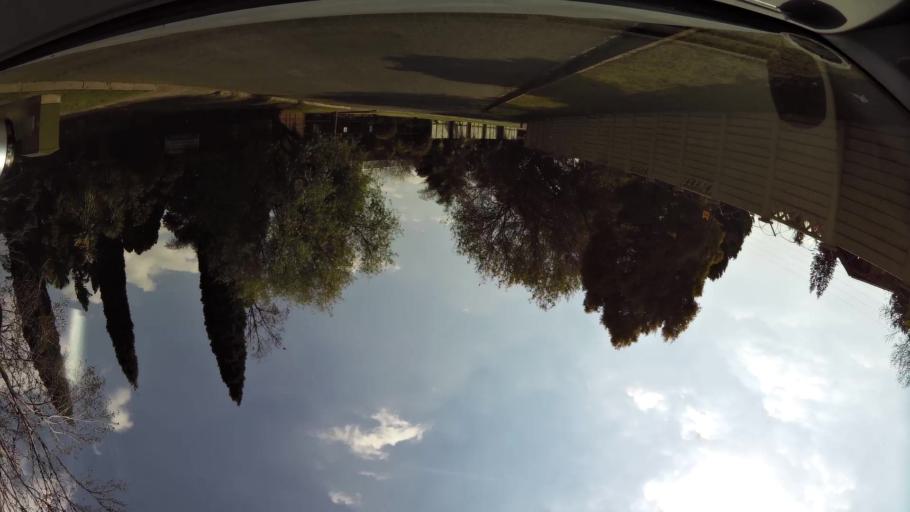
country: ZA
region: Gauteng
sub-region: City of Johannesburg Metropolitan Municipality
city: Modderfontein
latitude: -26.0891
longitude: 28.2270
